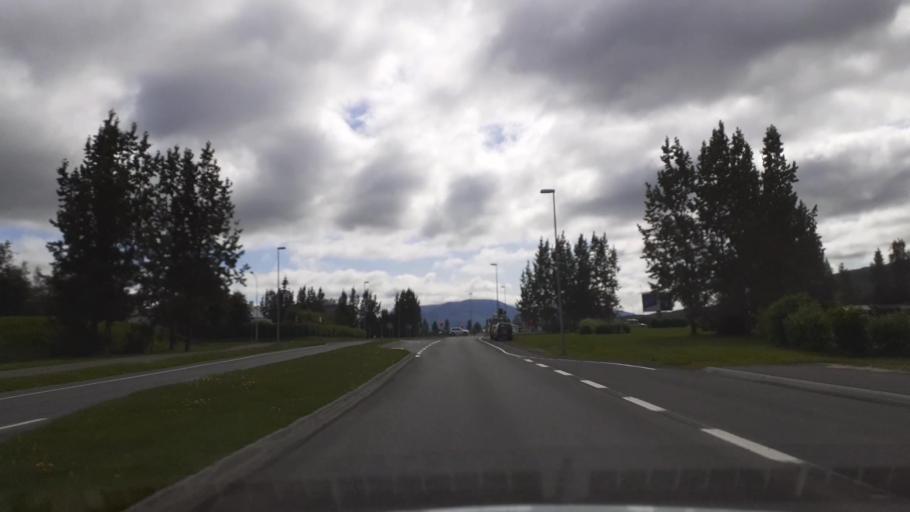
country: IS
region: Northeast
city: Akureyri
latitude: 65.6797
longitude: -18.1159
